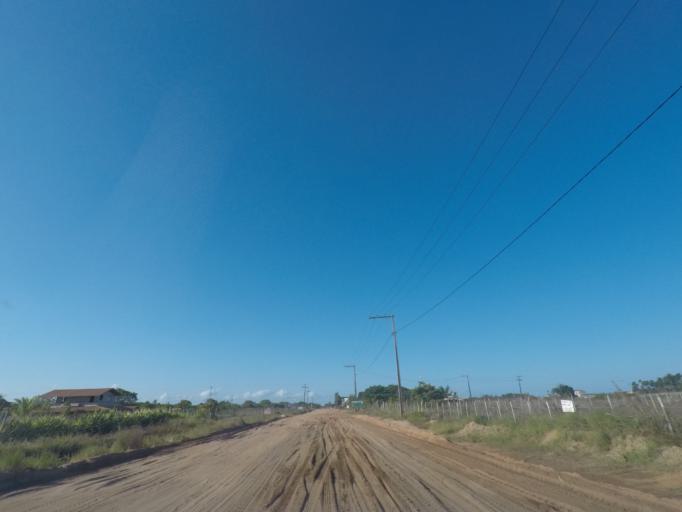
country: BR
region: Bahia
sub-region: Camamu
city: Camamu
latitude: -13.9341
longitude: -38.9471
